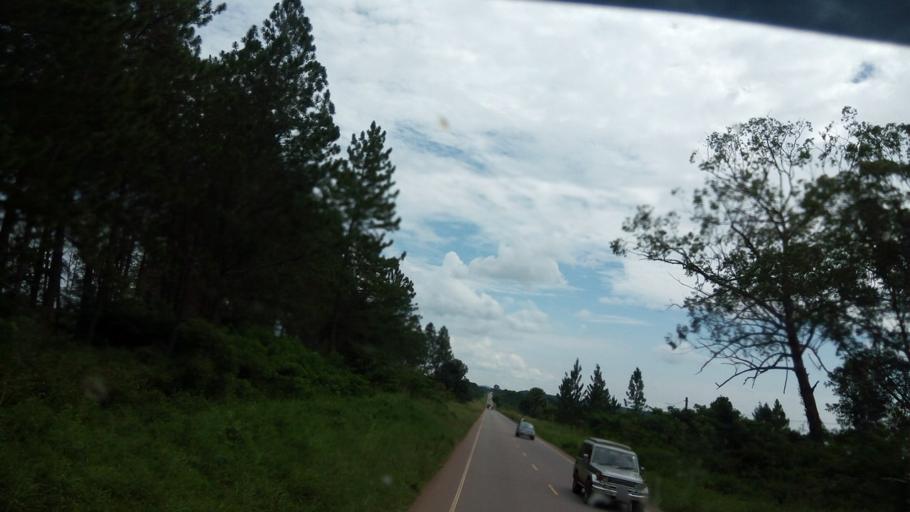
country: UG
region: Central Region
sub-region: Nakasongola District
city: Nakasongola
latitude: 1.1659
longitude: 32.4636
